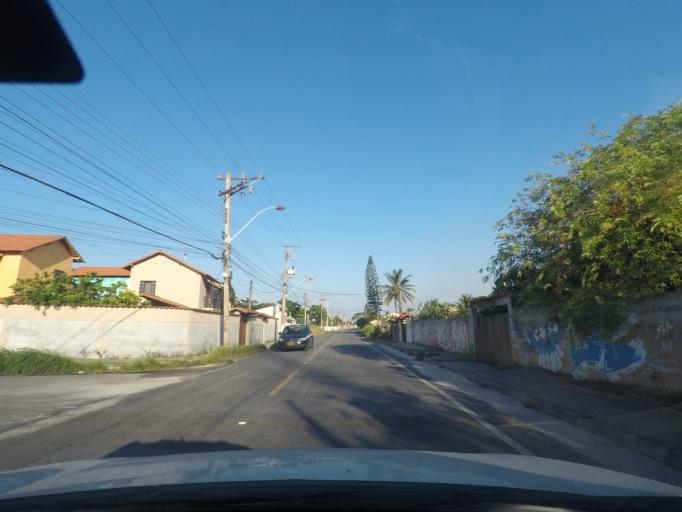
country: BR
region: Rio de Janeiro
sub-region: Marica
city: Marica
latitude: -22.9703
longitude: -42.9334
